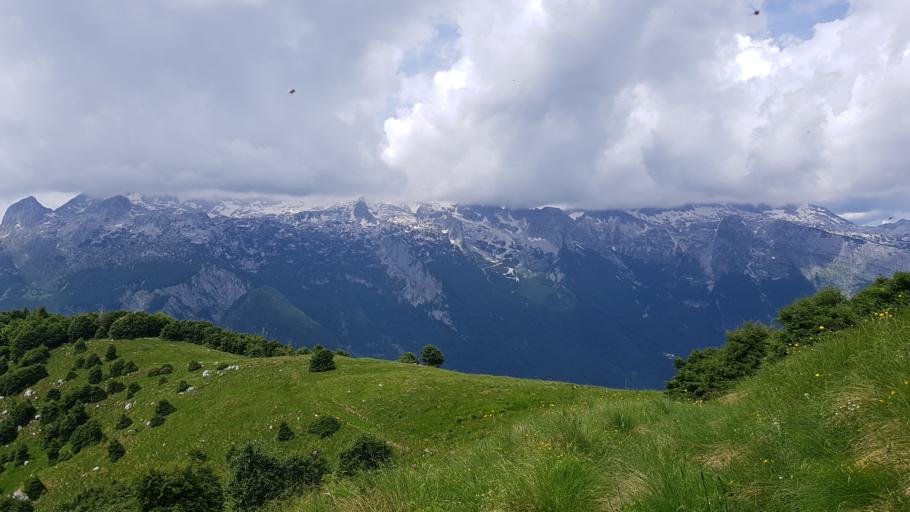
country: SI
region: Bovec
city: Bovec
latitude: 46.3025
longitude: 13.5190
